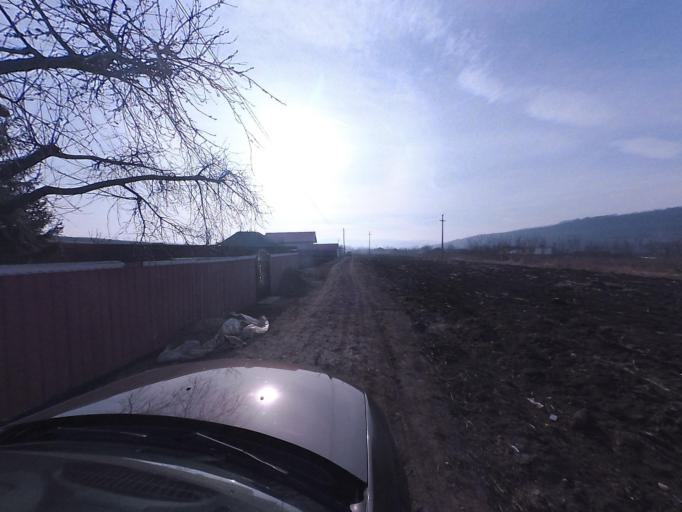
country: RO
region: Vaslui
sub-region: Comuna Solesti
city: Solesti
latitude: 46.8109
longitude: 27.7791
